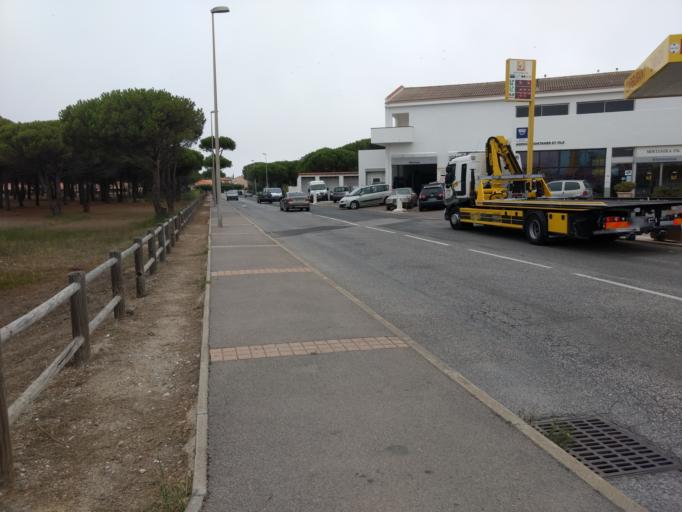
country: FR
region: Languedoc-Roussillon
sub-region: Departement des Pyrenees-Orientales
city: Le Barcares
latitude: 42.7831
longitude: 3.0337
